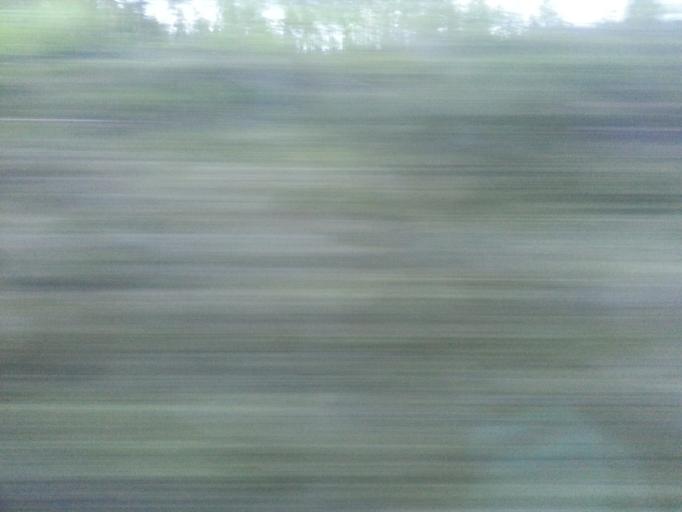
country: NO
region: Oppland
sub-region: Dovre
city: Dombas
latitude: 62.0853
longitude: 9.1407
